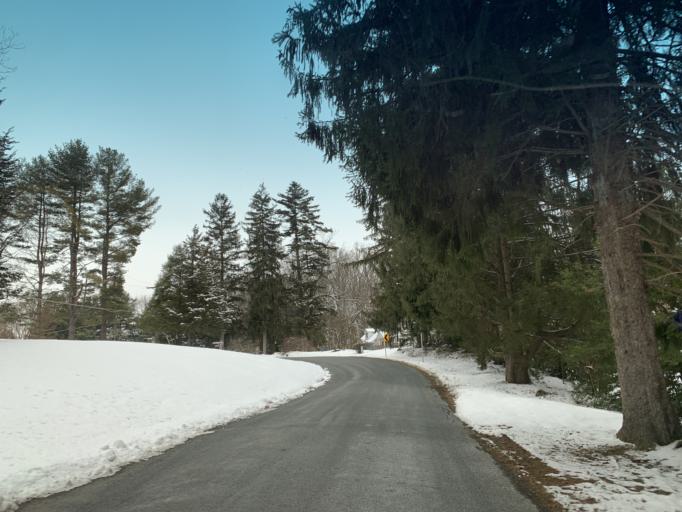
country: US
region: Maryland
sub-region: Harford County
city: Aberdeen
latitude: 39.5628
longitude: -76.1831
